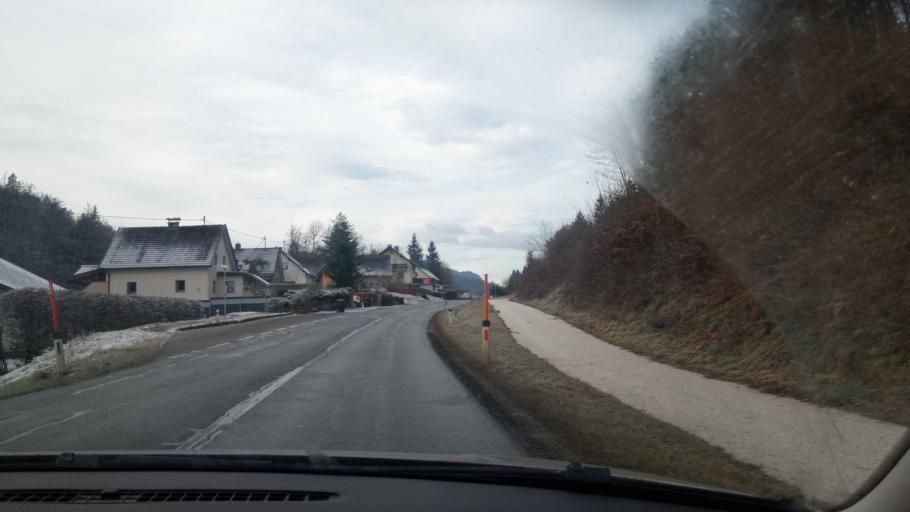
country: AT
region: Carinthia
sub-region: Politischer Bezirk Klagenfurt Land
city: Kottmannsdorf
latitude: 46.5891
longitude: 14.2486
